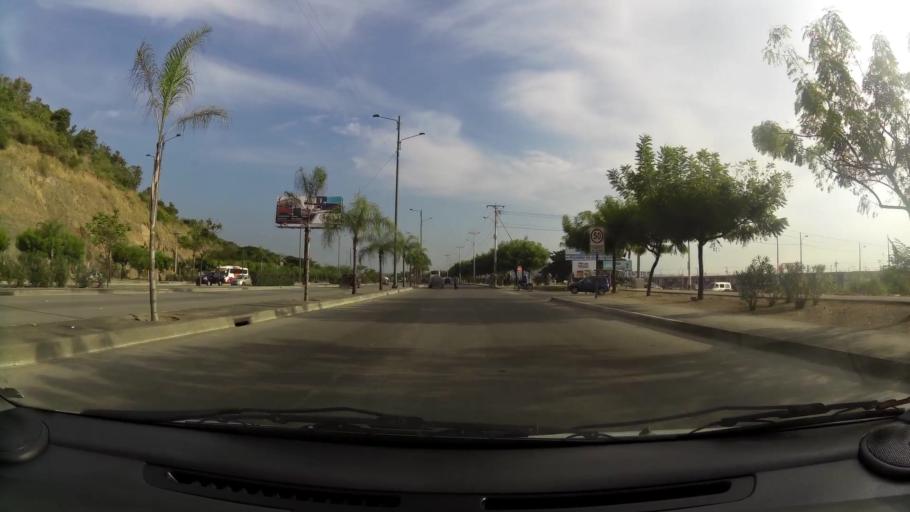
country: EC
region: Guayas
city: Eloy Alfaro
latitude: -2.0711
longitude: -79.8978
